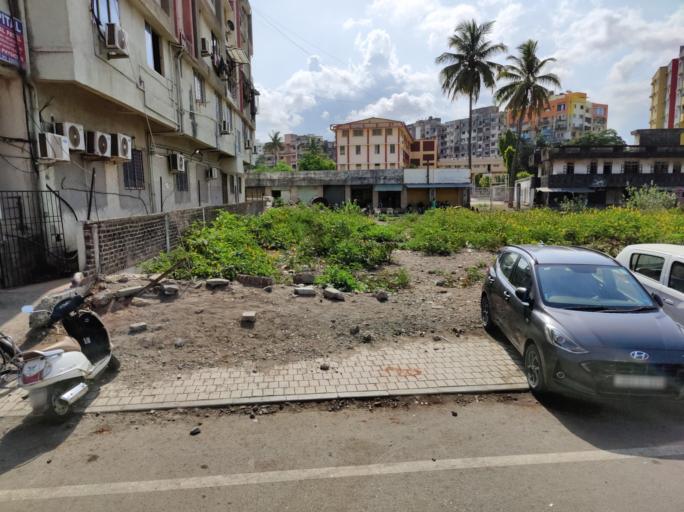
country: IN
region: Daman and Diu
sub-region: Daman District
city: Daman
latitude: 20.4180
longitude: 72.8375
